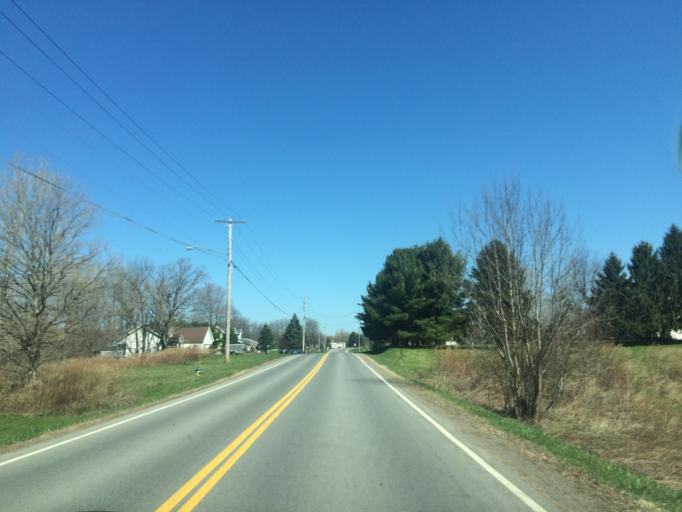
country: US
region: New York
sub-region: Wayne County
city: Palmyra
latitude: 43.0660
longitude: -77.2592
